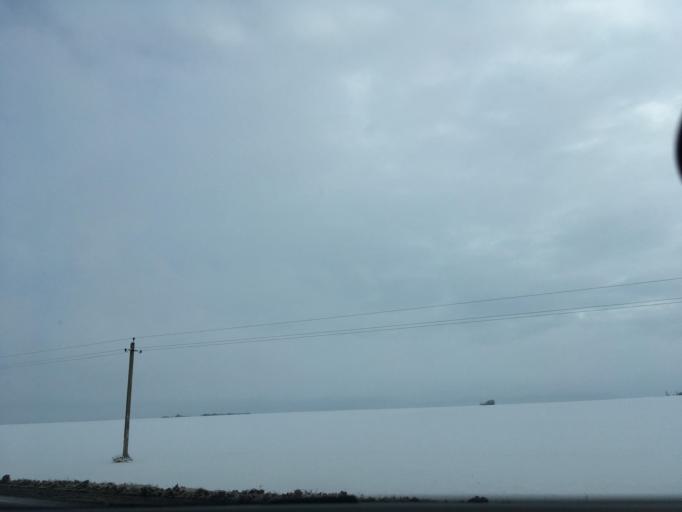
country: UA
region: Luhansk
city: Lozno-Oleksandrivka
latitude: 49.9513
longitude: 38.9561
